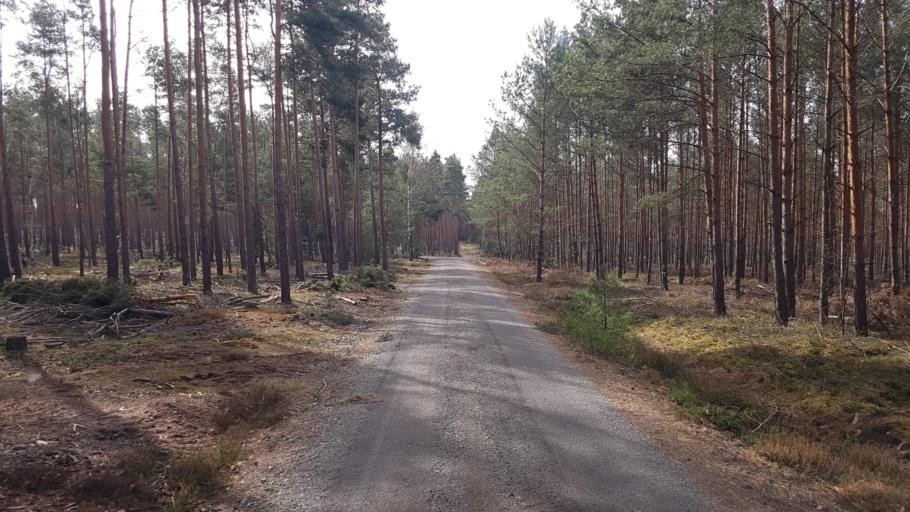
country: DE
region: Brandenburg
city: Elsterwerda
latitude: 51.4919
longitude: 13.4603
